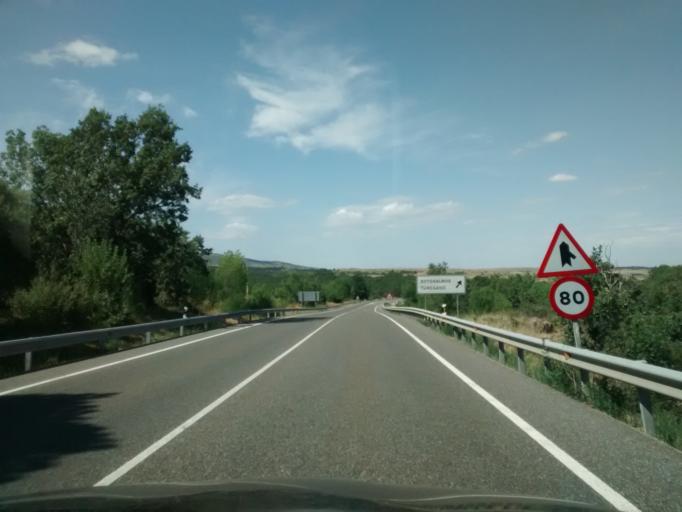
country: ES
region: Castille and Leon
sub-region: Provincia de Segovia
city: Sotosalbos
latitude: 41.0332
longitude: -3.9338
